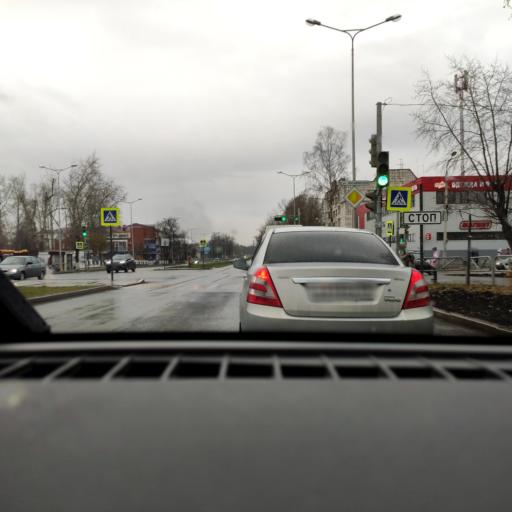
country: RU
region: Perm
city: Kultayevo
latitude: 58.0019
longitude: 55.9457
